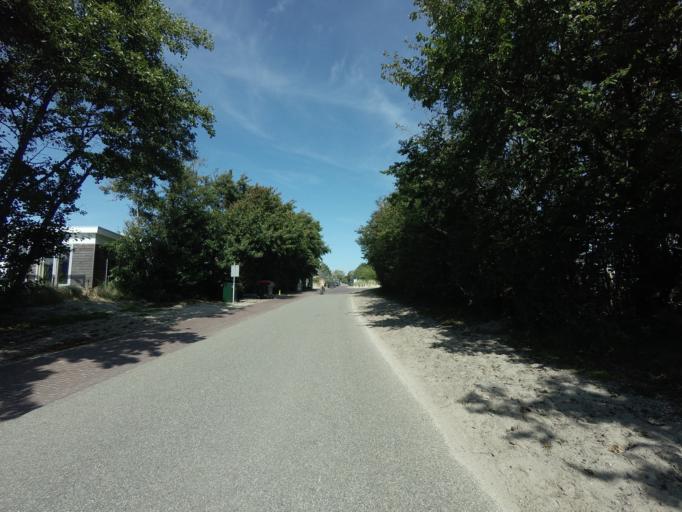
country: NL
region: Friesland
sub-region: Gemeente Ameland
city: Hollum
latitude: 53.4494
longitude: 5.6371
